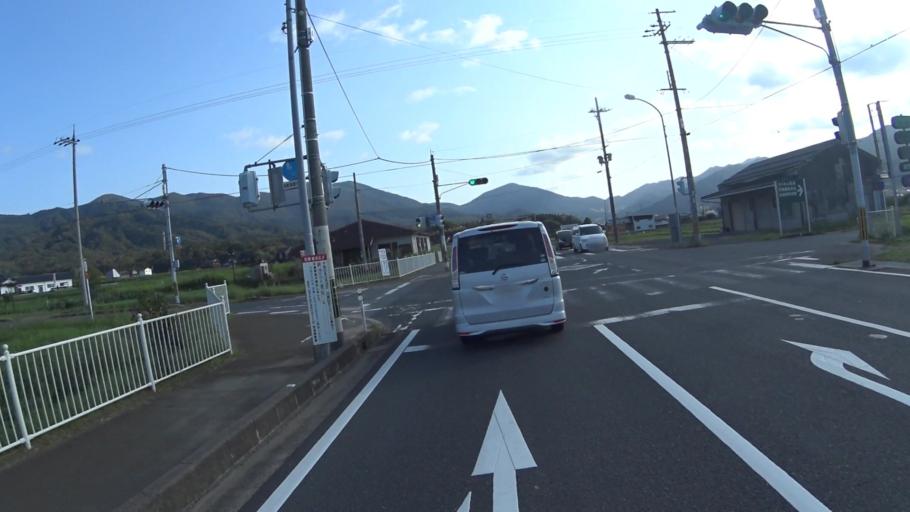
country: JP
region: Kyoto
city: Miyazu
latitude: 35.5038
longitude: 135.1037
